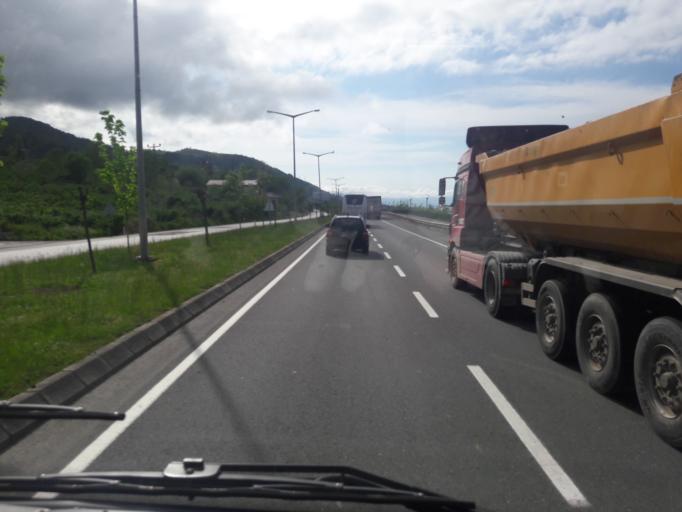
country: TR
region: Ordu
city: Gulyali
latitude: 40.9649
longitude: 38.0723
